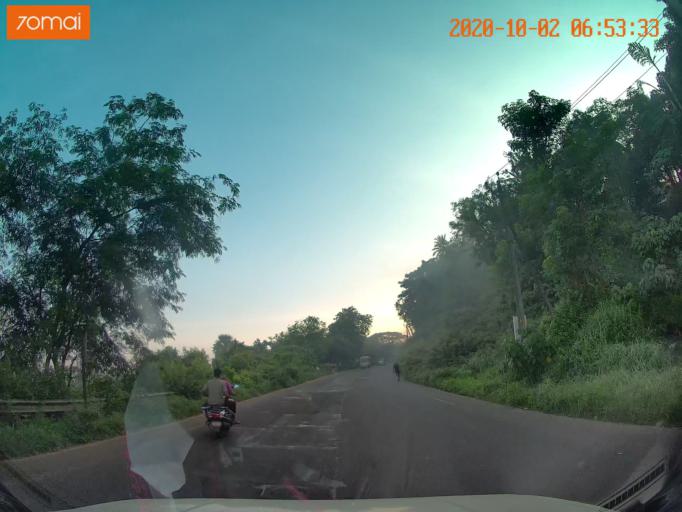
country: IN
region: Kerala
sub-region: Malappuram
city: Tirur
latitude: 10.8498
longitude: 76.0331
